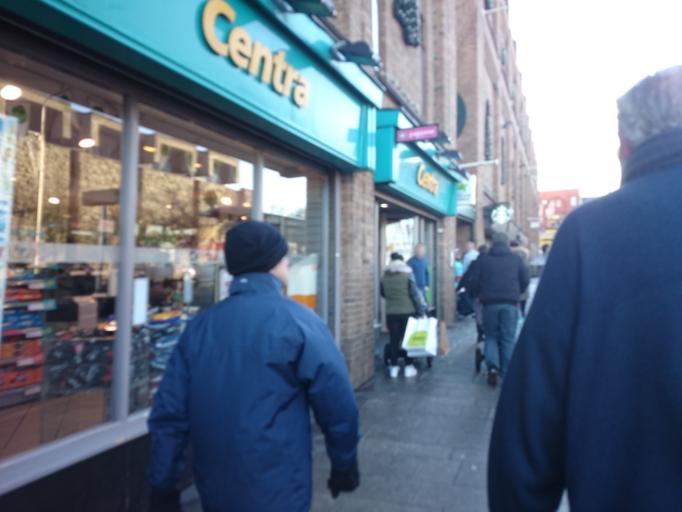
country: IE
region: Leinster
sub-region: Dun Laoghaire-Rathdown
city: Dun Laoghaire
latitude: 53.2929
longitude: -6.1353
